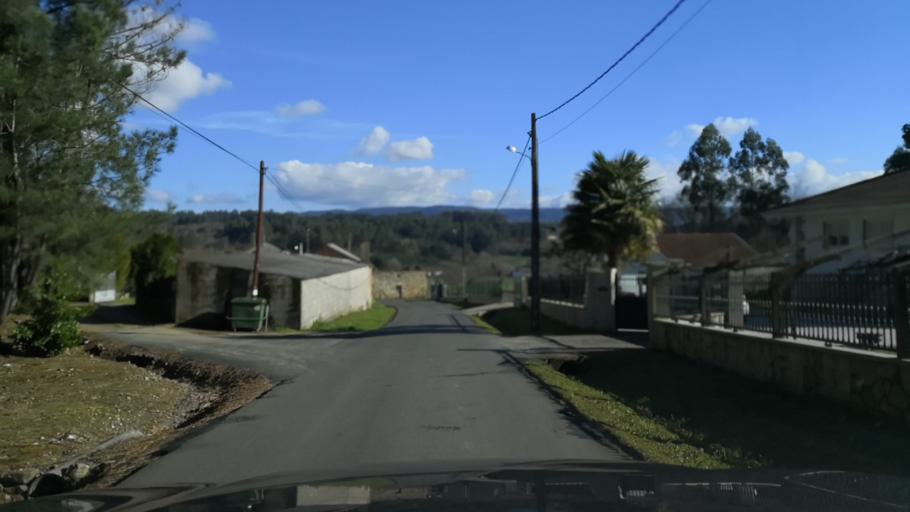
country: ES
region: Galicia
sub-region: Provincia da Coruna
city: Ribeira
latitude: 42.7164
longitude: -8.4395
